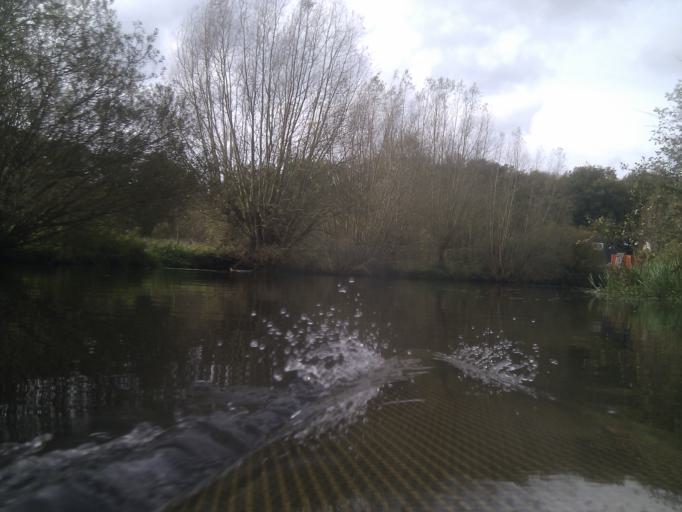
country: NL
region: Utrecht
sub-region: Gemeente Bunnik
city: Bunnik
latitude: 52.0881
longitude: 5.2012
